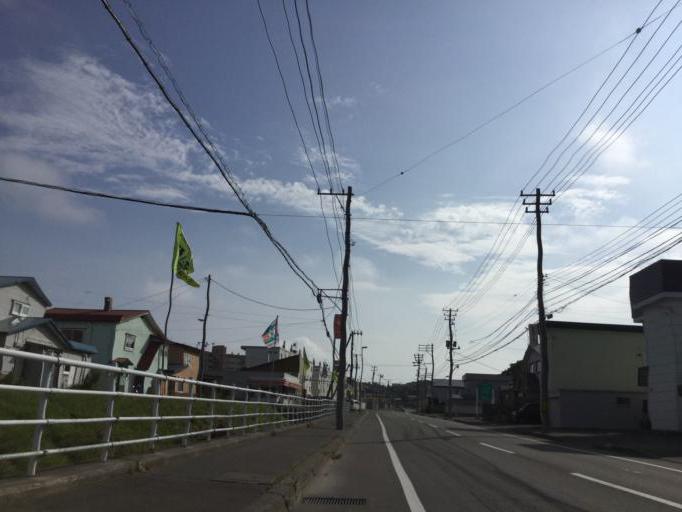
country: JP
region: Hokkaido
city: Wakkanai
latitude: 45.3883
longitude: 141.6767
